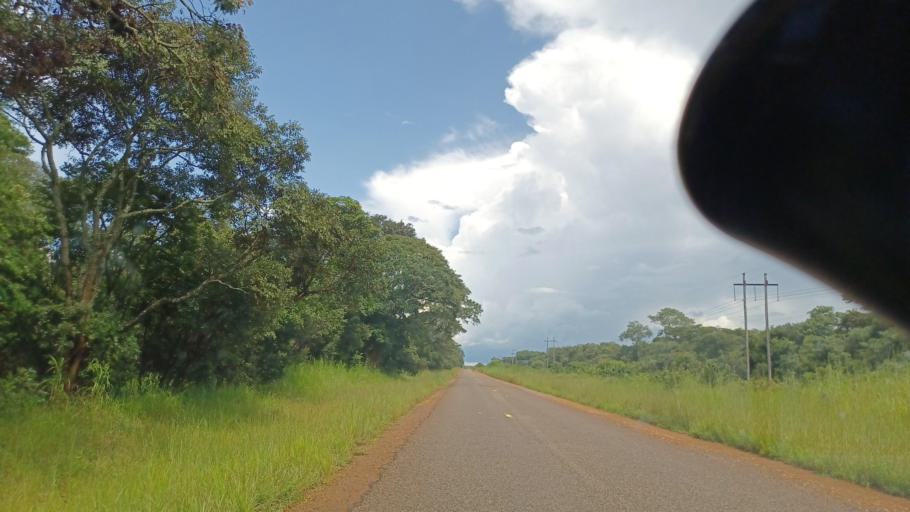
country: ZM
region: North-Western
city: Kasempa
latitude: -12.8935
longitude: 26.0520
